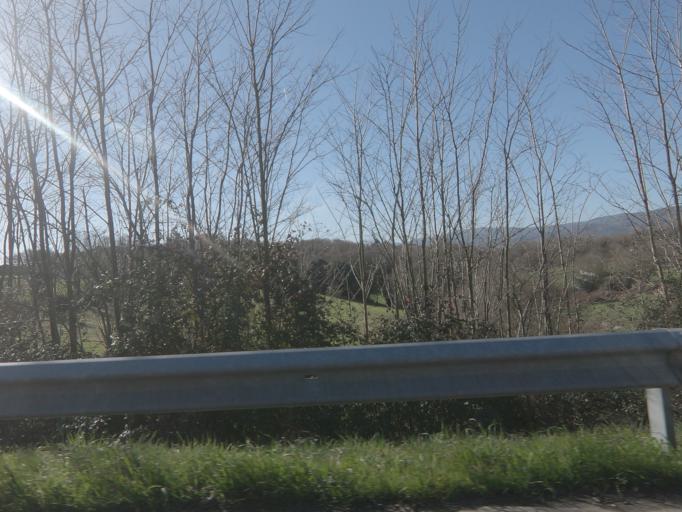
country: ES
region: Galicia
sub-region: Provincia de Pontevedra
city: Lalin
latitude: 42.6825
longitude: -8.1686
